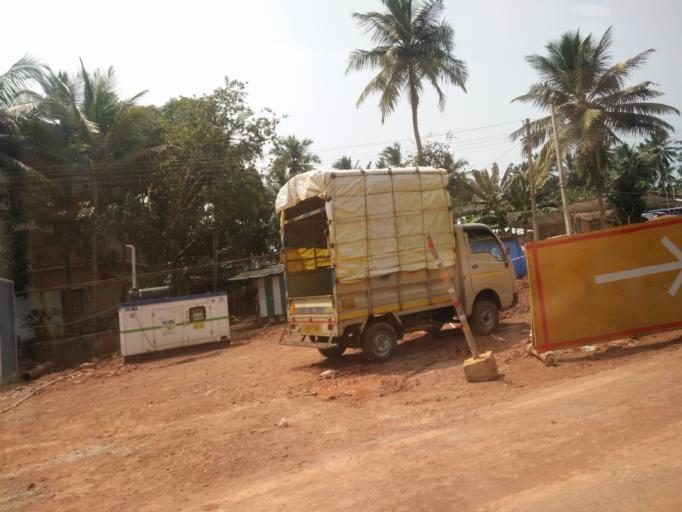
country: IN
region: Goa
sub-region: South Goa
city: Cortalim
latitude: 15.3991
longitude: 73.9098
